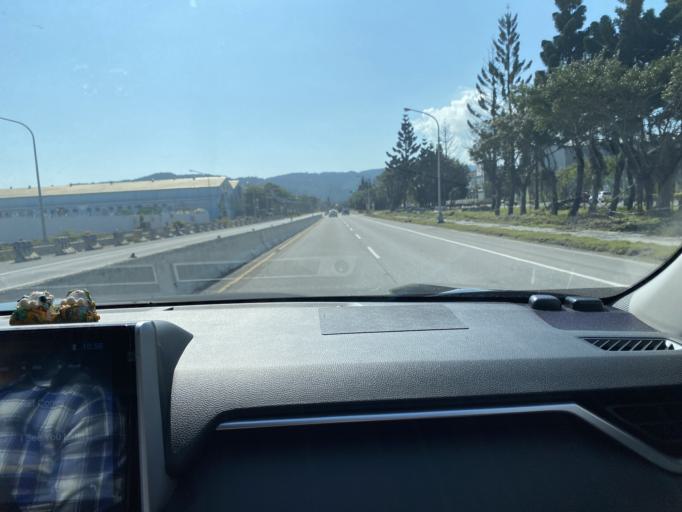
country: TW
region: Taiwan
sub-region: Hualien
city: Hualian
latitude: 23.9352
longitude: 121.5944
